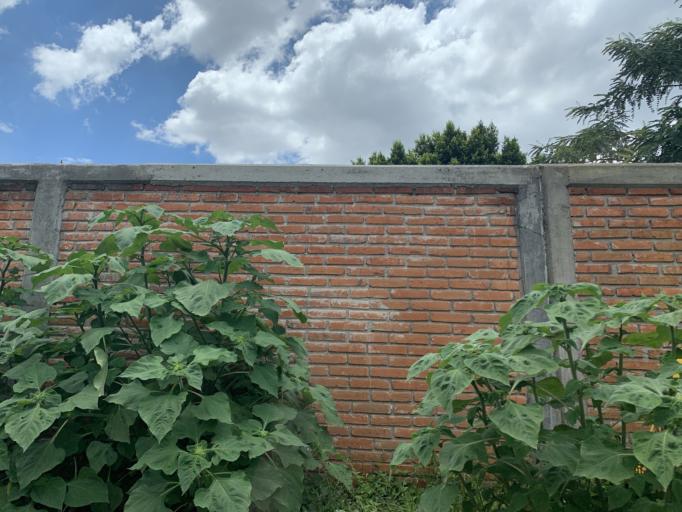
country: MX
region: Puebla
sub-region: Cuautlancingo
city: Sanctorum
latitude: 19.0890
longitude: -98.2447
